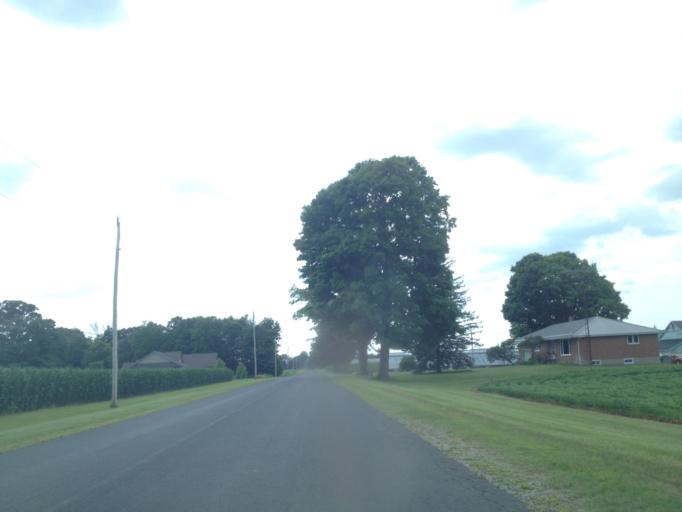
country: CA
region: Ontario
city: Aylmer
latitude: 42.6812
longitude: -81.0015
